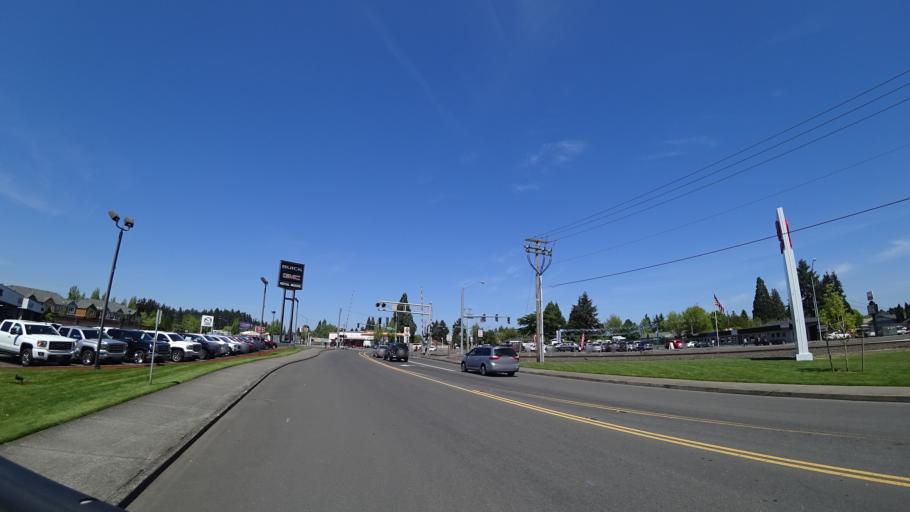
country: US
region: Oregon
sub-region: Washington County
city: Hillsboro
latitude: 45.5093
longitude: -122.9687
